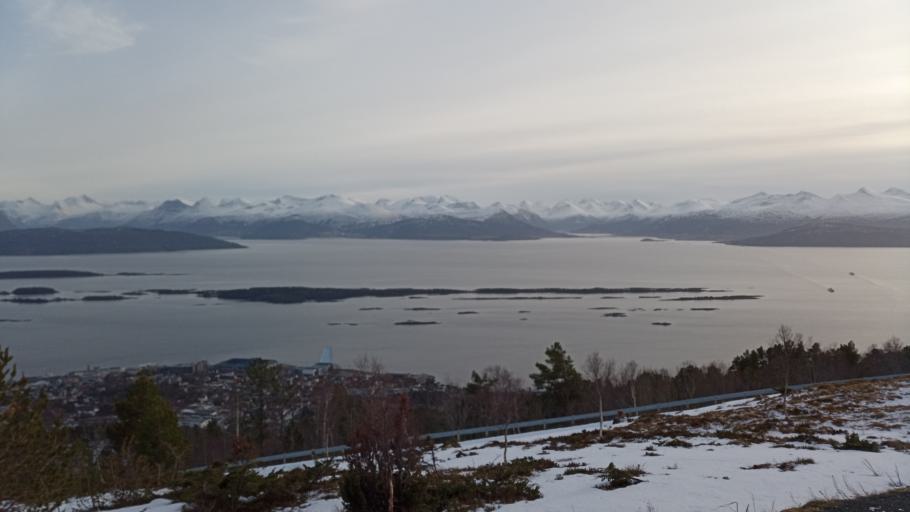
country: NO
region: More og Romsdal
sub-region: Molde
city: Molde
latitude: 62.7496
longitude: 7.1309
